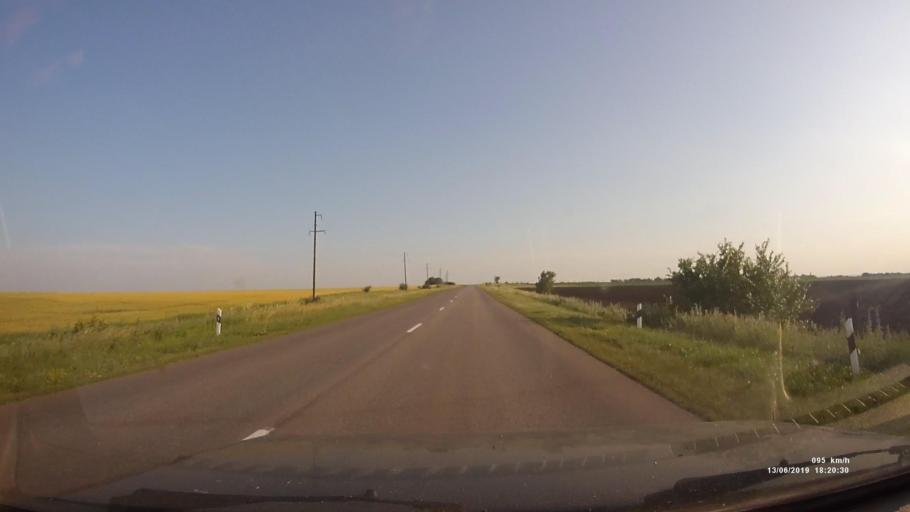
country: RU
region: Rostov
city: Kazanskaya
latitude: 49.8829
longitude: 41.2987
